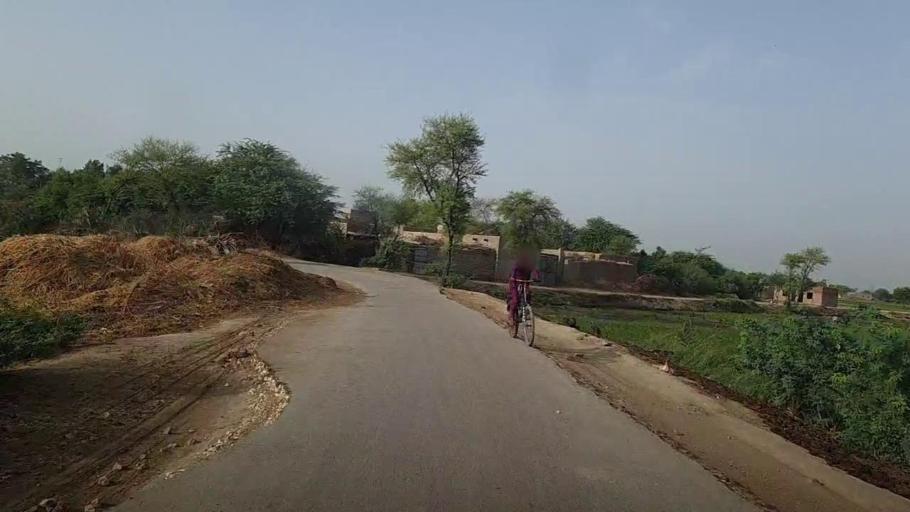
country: PK
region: Sindh
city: Khairpur Nathan Shah
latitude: 27.1185
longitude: 67.7878
